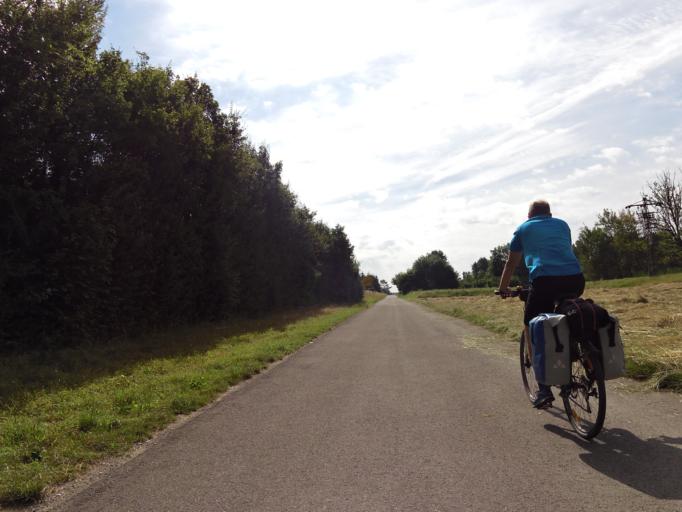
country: DE
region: Baden-Wuerttemberg
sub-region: Freiburg Region
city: Allensbach
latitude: 47.7303
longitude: 9.0262
